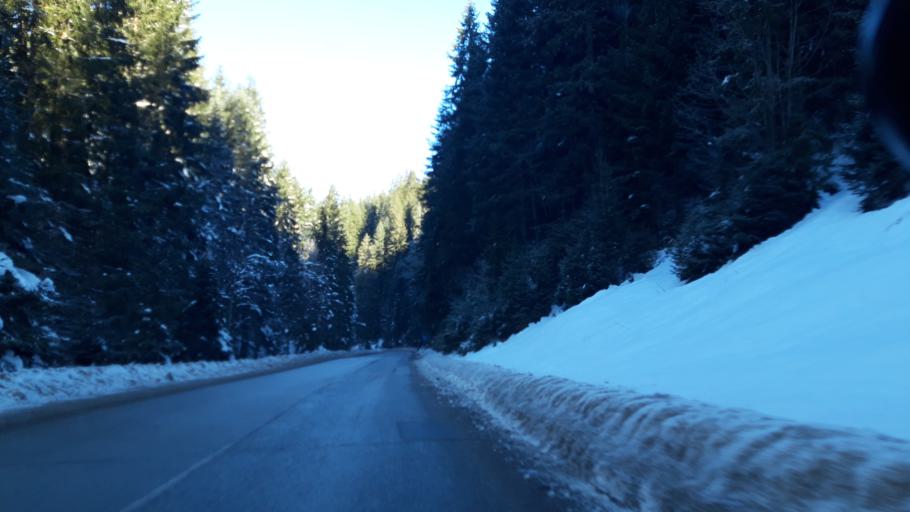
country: BA
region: Republika Srpska
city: Koran
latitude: 43.7605
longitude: 18.5486
